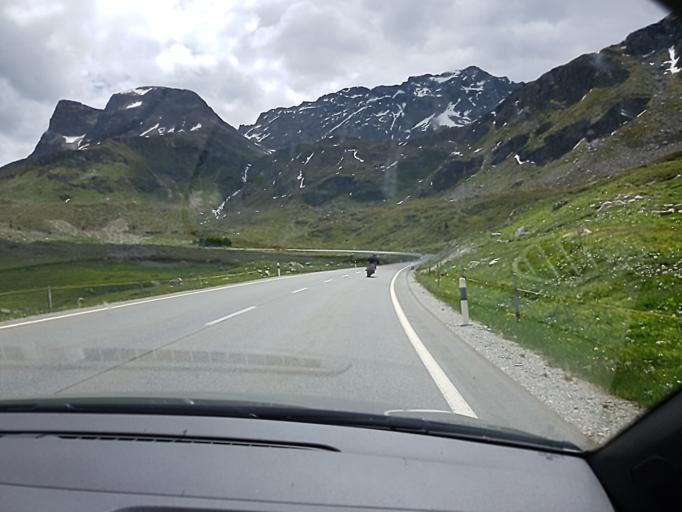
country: CH
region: Grisons
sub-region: Maloja District
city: Silvaplana
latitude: 46.4665
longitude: 9.6970
